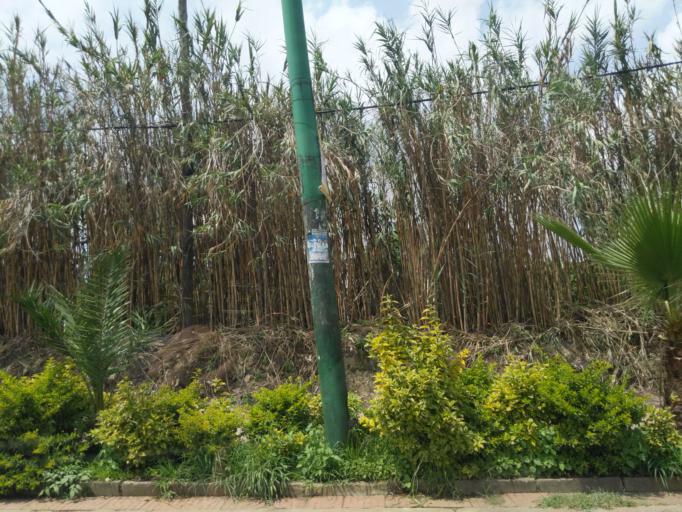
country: ET
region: Adis Abeba
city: Addis Ababa
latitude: 8.9614
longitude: 38.7637
